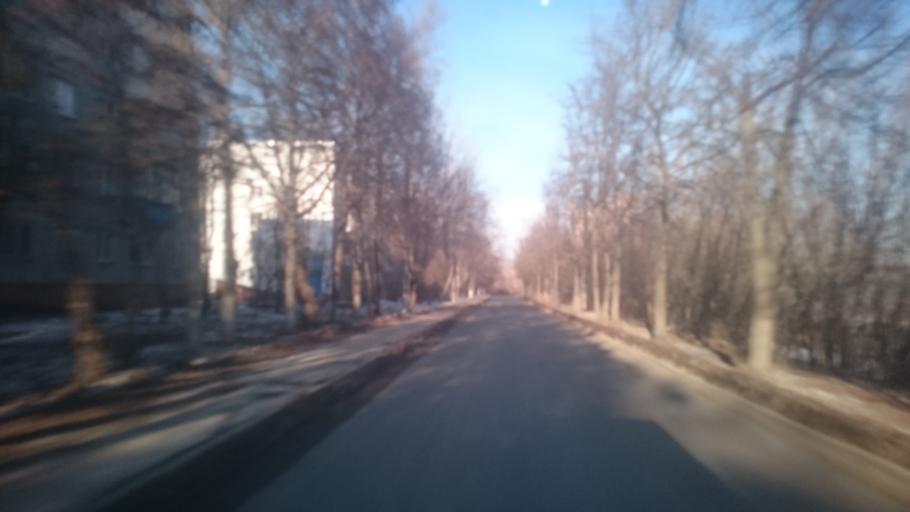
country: RU
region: Tula
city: Tula
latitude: 54.1780
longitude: 37.6420
